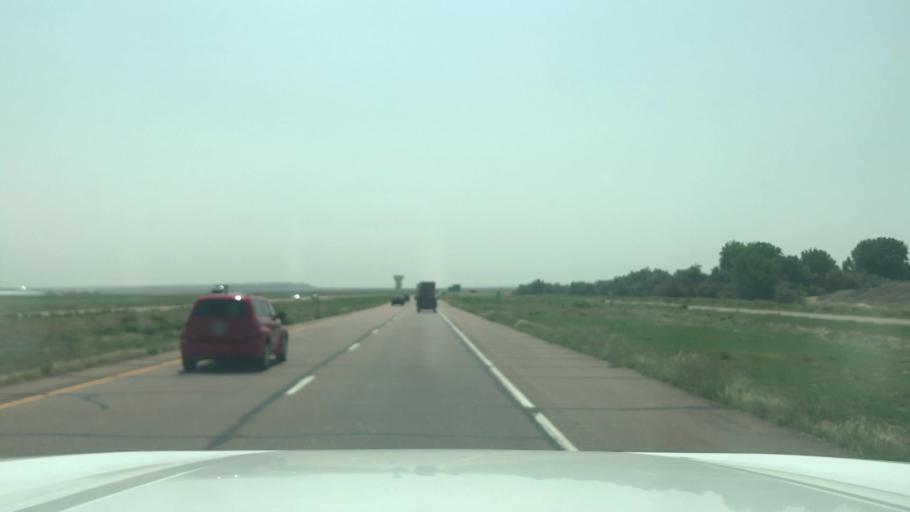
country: US
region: Colorado
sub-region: Pueblo County
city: Pueblo
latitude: 38.1796
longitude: -104.6342
